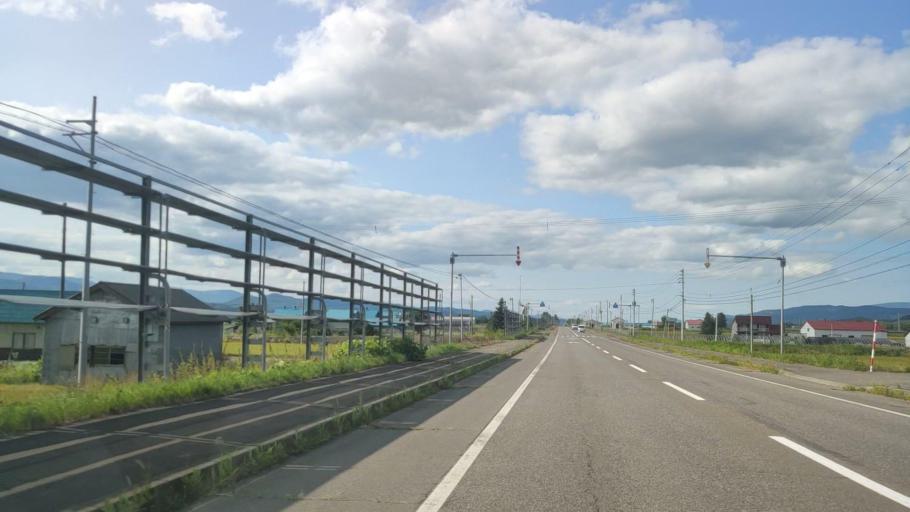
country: JP
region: Hokkaido
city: Nayoro
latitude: 44.4594
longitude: 142.3572
